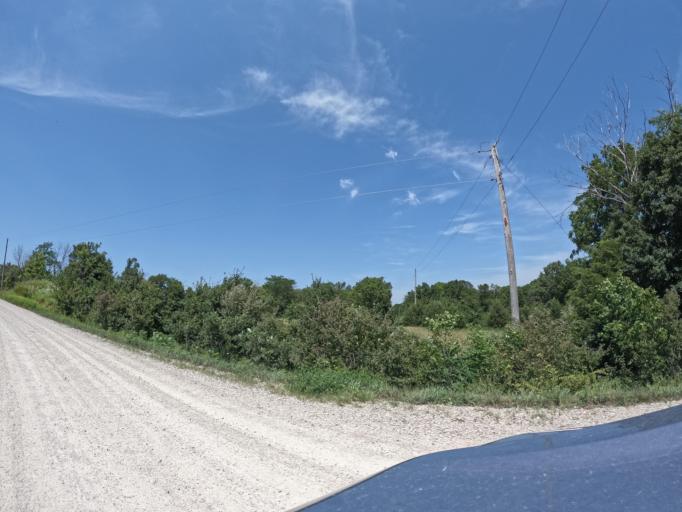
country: US
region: Iowa
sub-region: Henry County
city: Mount Pleasant
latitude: 40.9156
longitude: -91.6597
